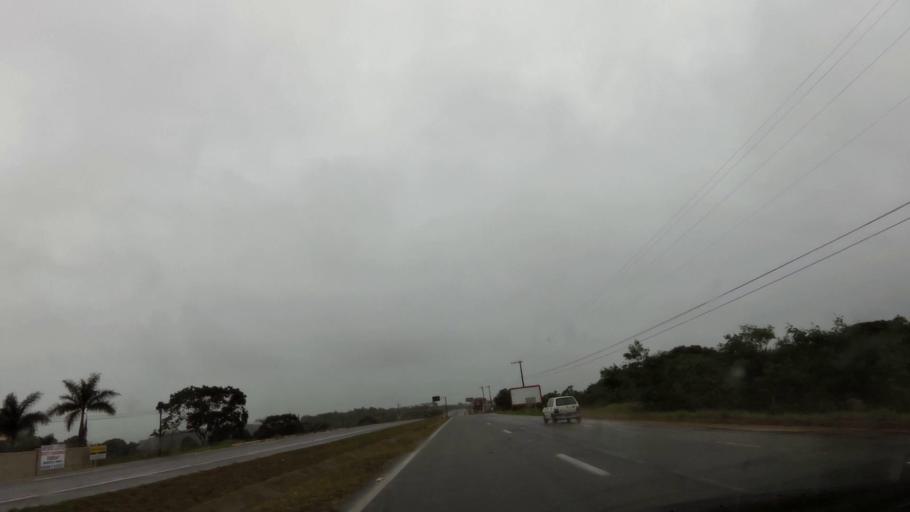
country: BR
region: Espirito Santo
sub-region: Guarapari
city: Guarapari
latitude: -20.5381
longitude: -40.3894
